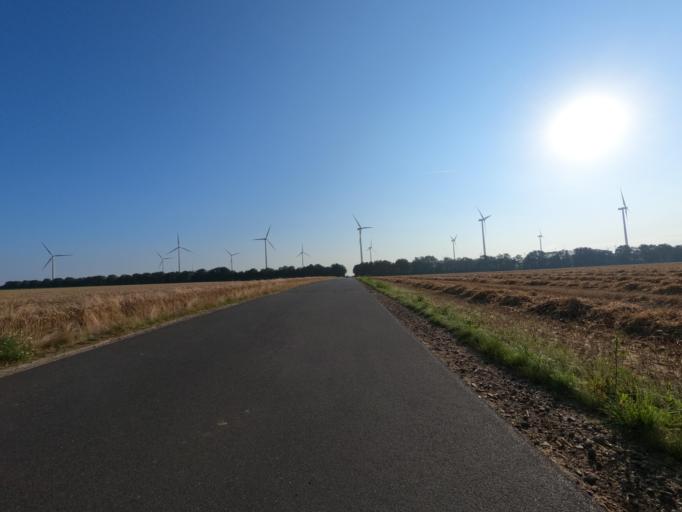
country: DE
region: North Rhine-Westphalia
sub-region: Regierungsbezirk Koln
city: Titz
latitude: 51.0216
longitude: 6.4808
